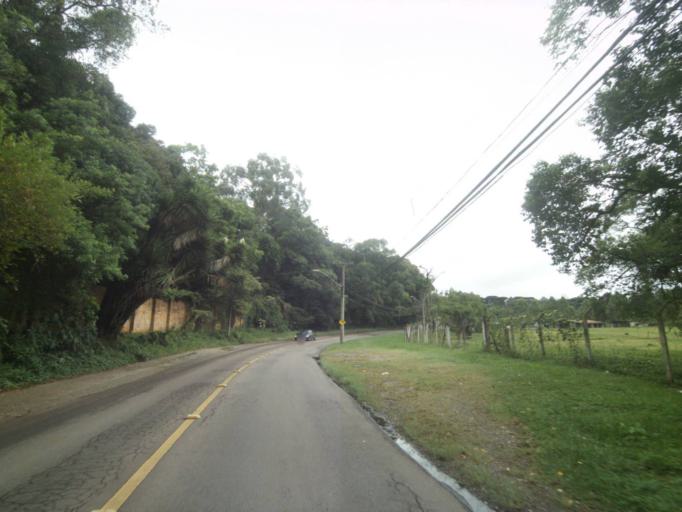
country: BR
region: Parana
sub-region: Curitiba
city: Curitiba
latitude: -25.4508
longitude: -49.3253
